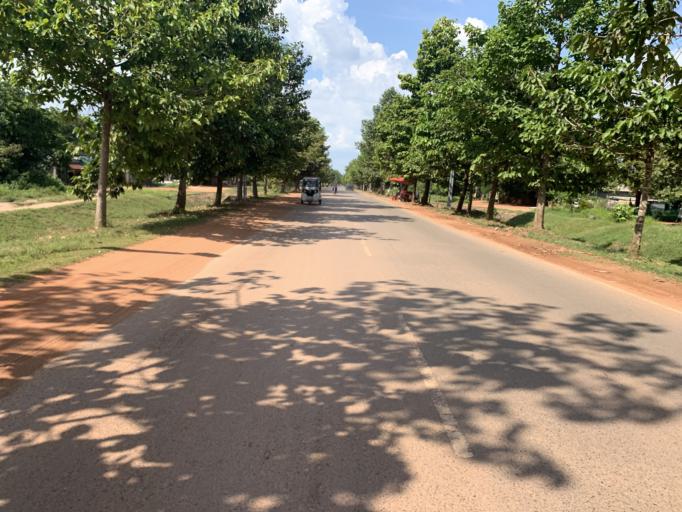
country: KH
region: Siem Reap
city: Siem Reap
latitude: 13.3852
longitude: 103.8793
